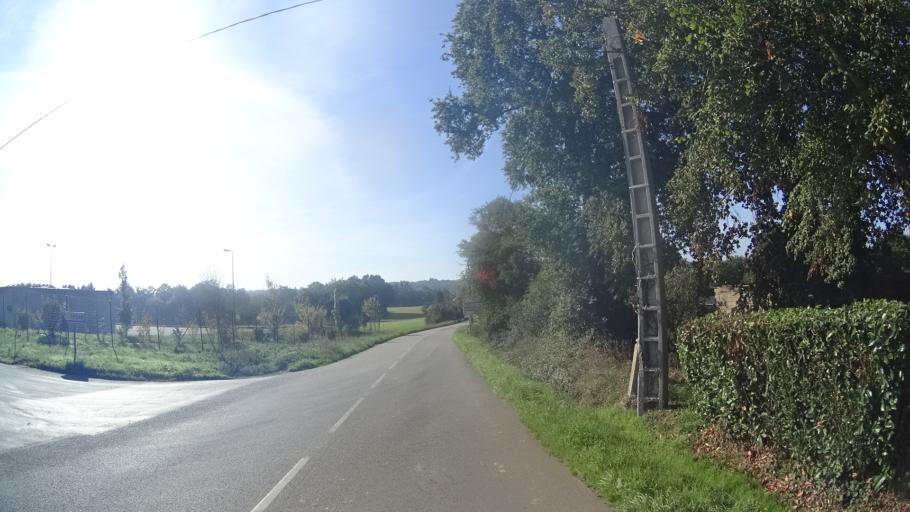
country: FR
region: Brittany
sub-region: Departement du Morbihan
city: Peillac
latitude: 47.7362
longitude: -2.2113
